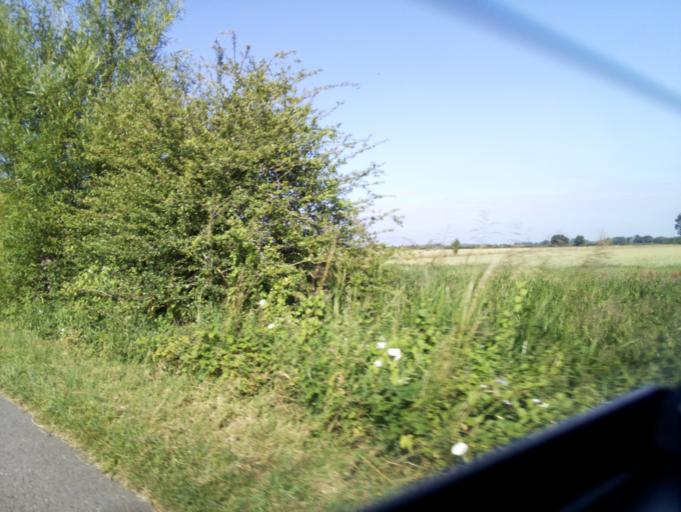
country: GB
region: England
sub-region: Oxfordshire
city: Bampton
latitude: 51.7090
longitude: -1.5012
